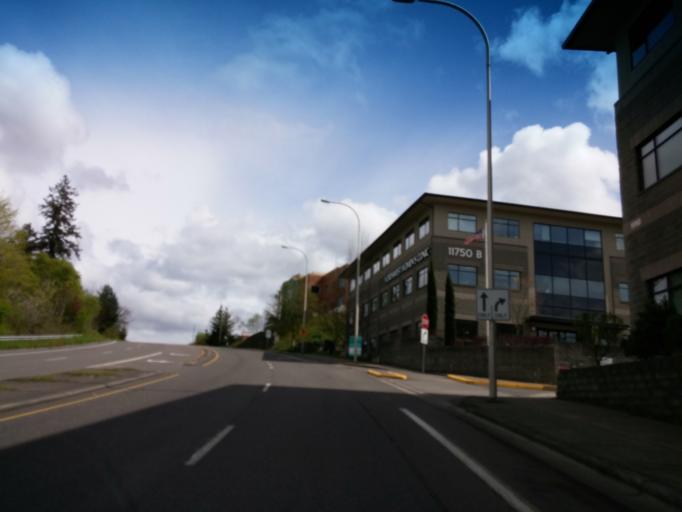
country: US
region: Oregon
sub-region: Washington County
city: Cedar Hills
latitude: 45.5177
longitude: -122.7983
